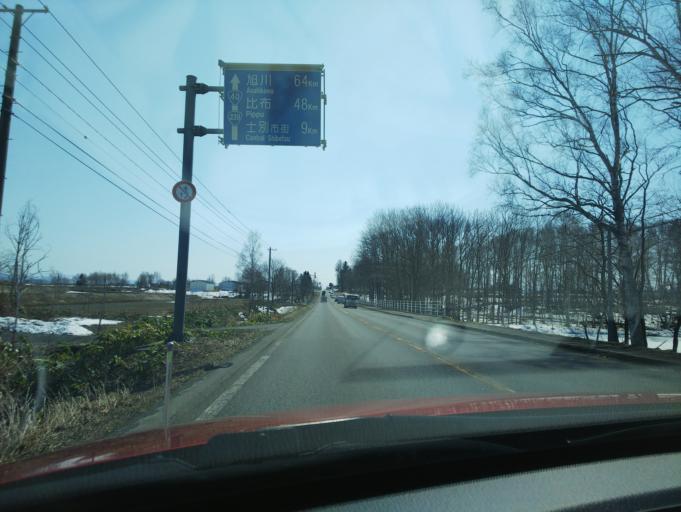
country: JP
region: Hokkaido
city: Nayoro
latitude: 44.2534
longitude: 142.3947
